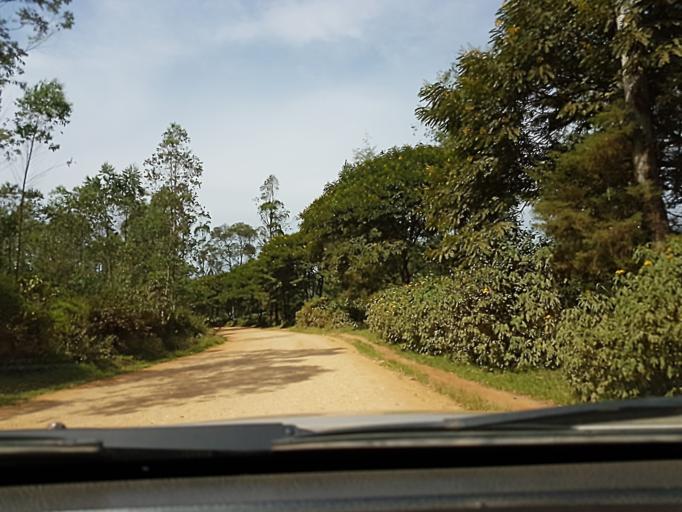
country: CD
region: South Kivu
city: Bukavu
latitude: -2.6452
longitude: 28.8742
